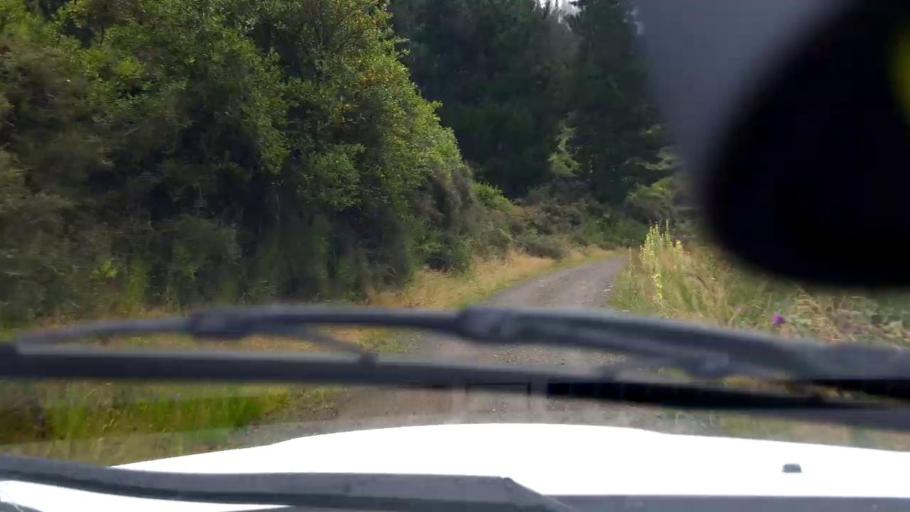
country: NZ
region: Canterbury
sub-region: Timaru District
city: Pleasant Point
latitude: -44.0332
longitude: 170.9953
